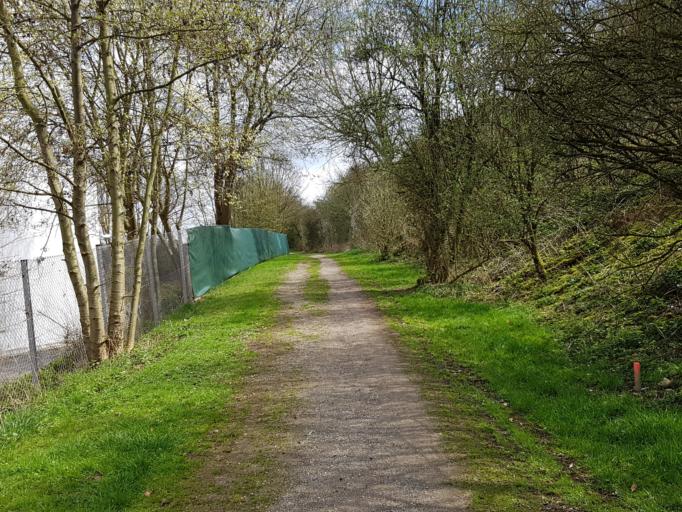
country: DE
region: North Rhine-Westphalia
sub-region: Regierungsbezirk Koln
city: Wurselen
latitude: 50.7878
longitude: 6.1404
